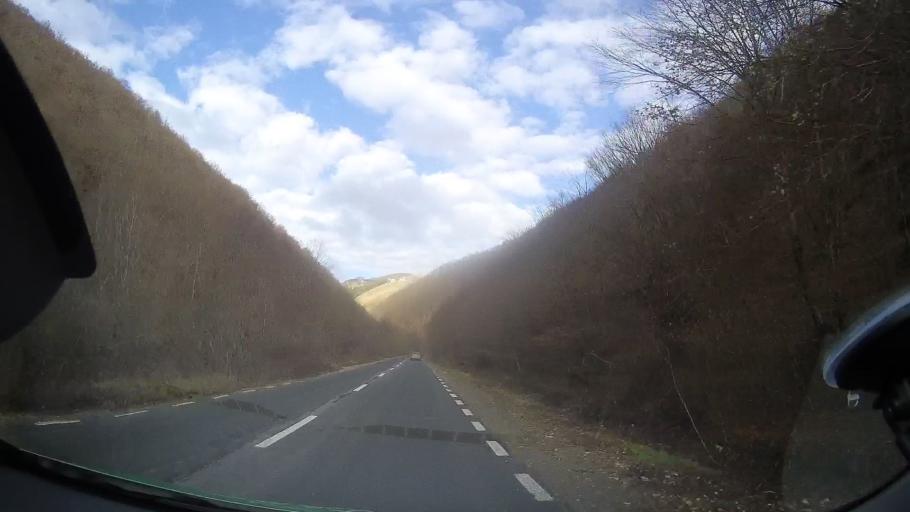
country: RO
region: Cluj
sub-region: Comuna Baisoara
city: Baisoara
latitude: 46.5875
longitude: 23.4421
